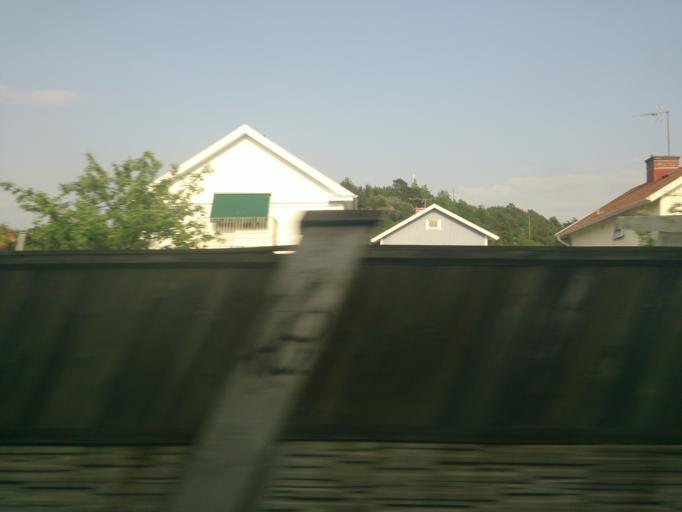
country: SE
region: Halland
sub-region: Kungsbacka Kommun
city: Kungsbacka
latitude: 57.4955
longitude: 12.0802
